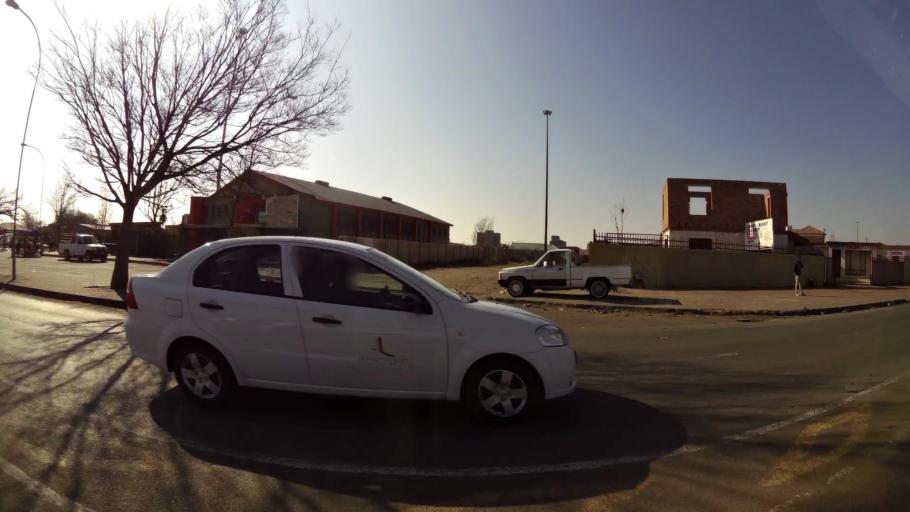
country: ZA
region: Orange Free State
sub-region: Mangaung Metropolitan Municipality
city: Bloemfontein
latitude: -29.1409
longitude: 26.2376
